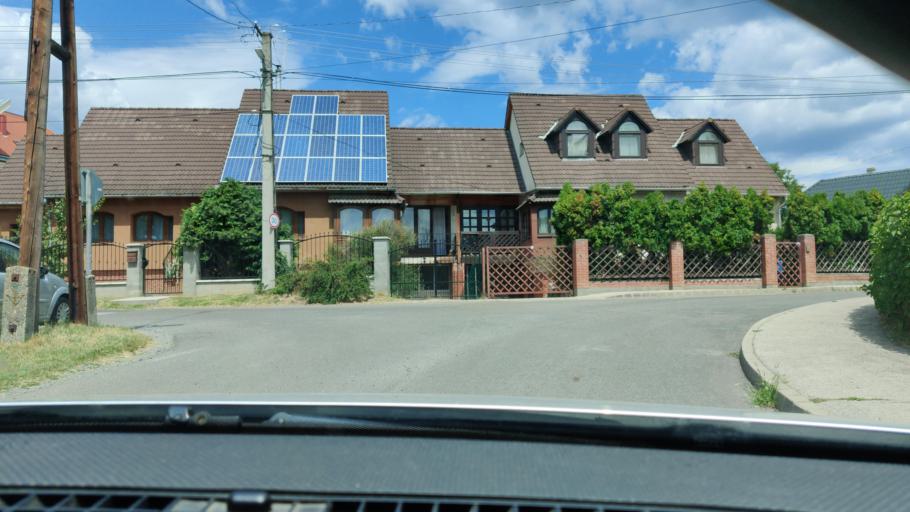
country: HU
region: Baranya
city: Pecs
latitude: 46.0856
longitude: 18.2620
